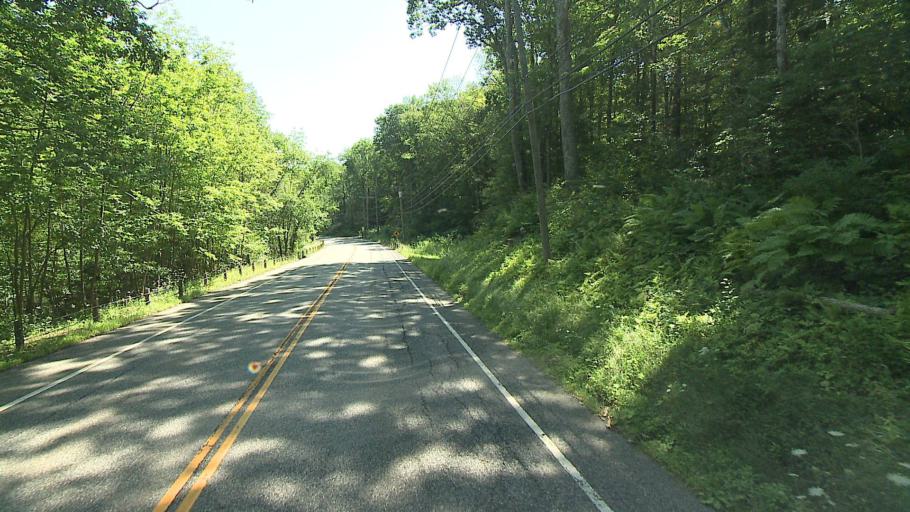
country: US
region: Connecticut
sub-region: Litchfield County
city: Kent
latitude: 41.8219
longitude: -73.4023
